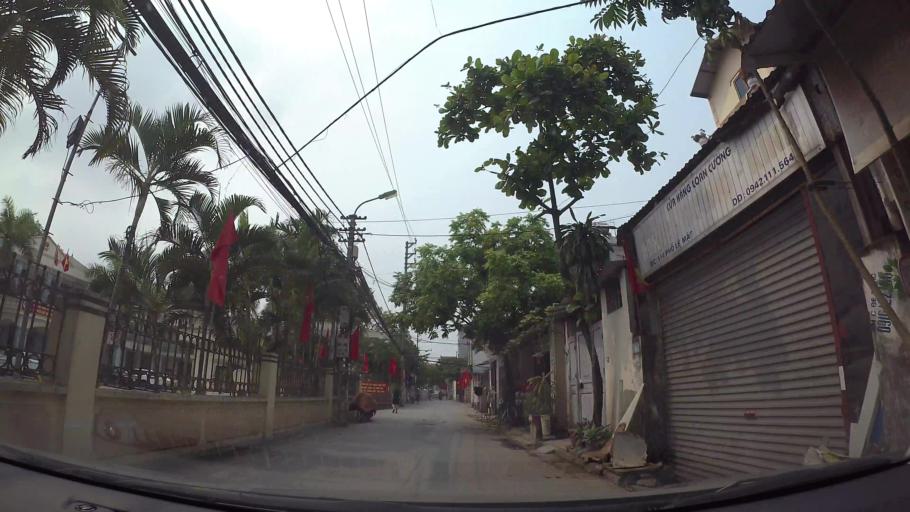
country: VN
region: Ha Noi
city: Trau Quy
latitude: 21.0573
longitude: 105.8988
